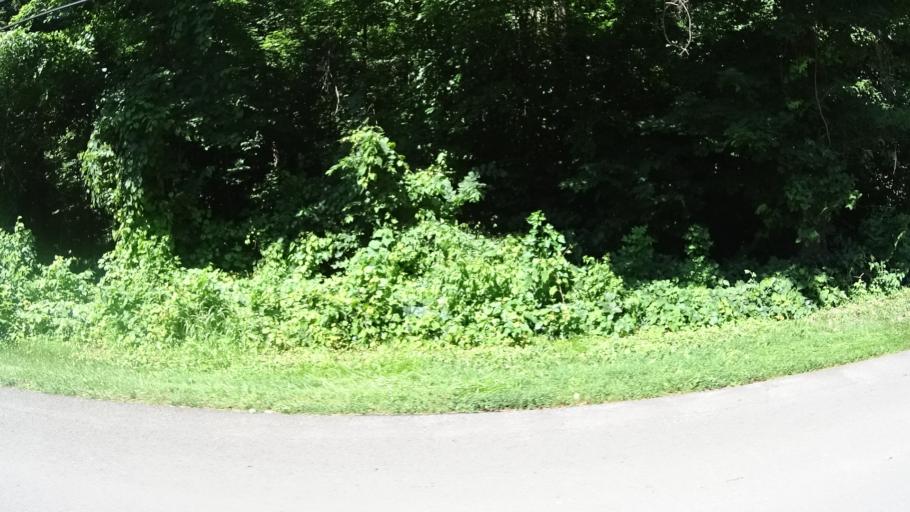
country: US
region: Ohio
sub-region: Ottawa County
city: Port Clinton
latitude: 41.4411
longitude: -82.8430
